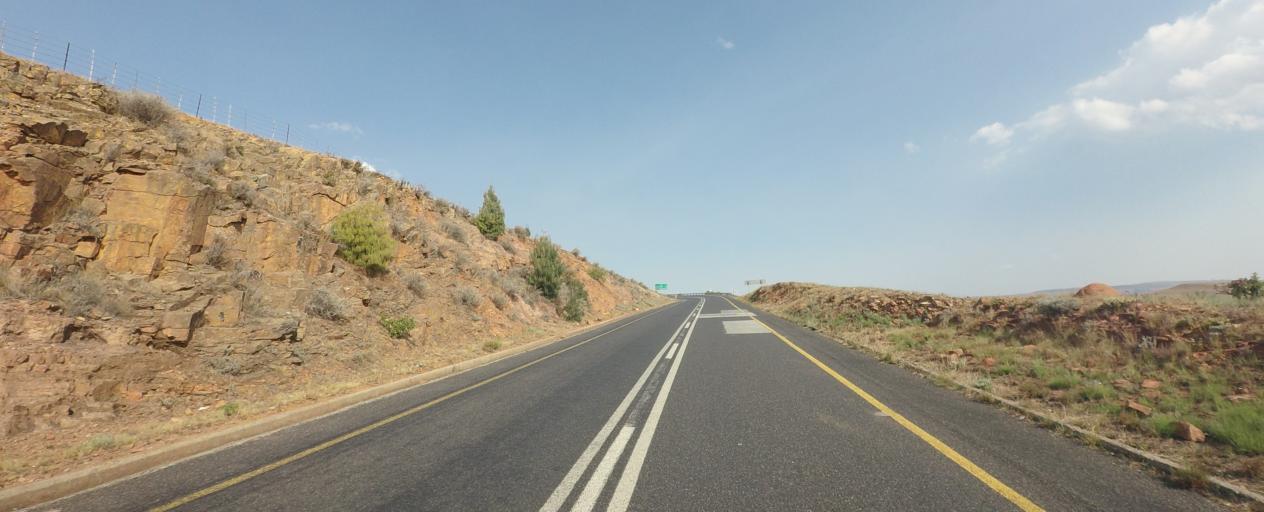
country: ZA
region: Mpumalanga
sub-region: Ehlanzeni District
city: Lydenburg
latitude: -25.1043
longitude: 30.5388
